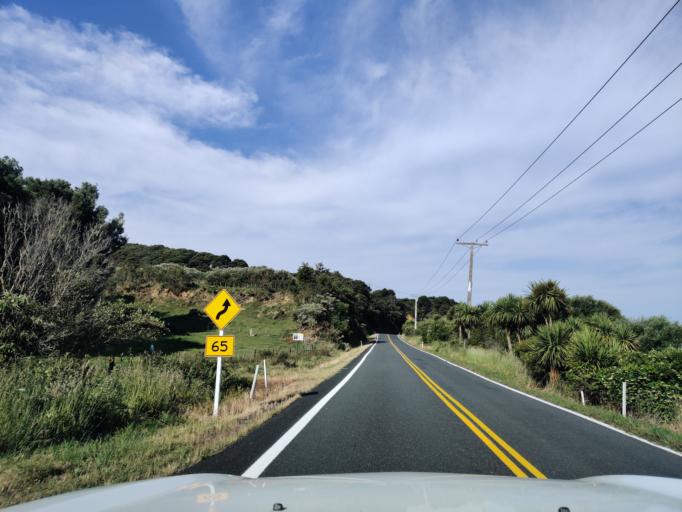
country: NZ
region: Waikato
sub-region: Waikato District
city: Ngaruawahia
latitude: -37.6328
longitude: 175.1552
